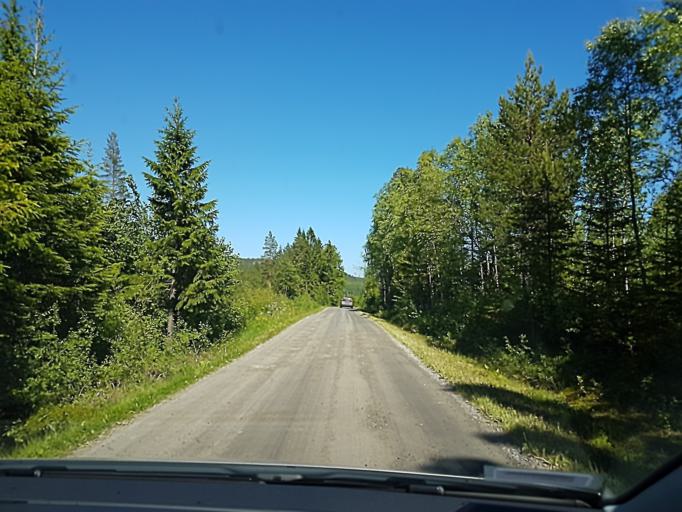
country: SE
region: Vaesternorrland
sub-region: OErnskoeldsviks Kommun
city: Bjasta
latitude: 63.0776
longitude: 18.4572
